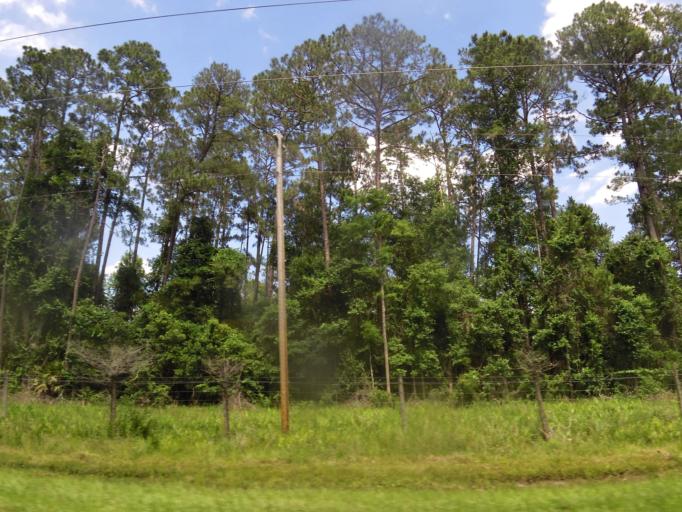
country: US
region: Florida
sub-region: Clay County
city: Green Cove Springs
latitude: 29.9744
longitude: -81.7394
